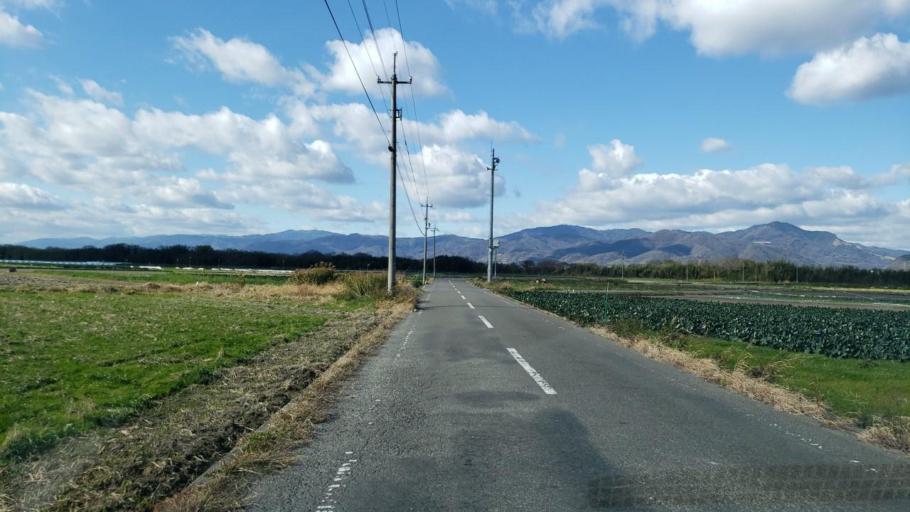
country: JP
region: Tokushima
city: Kamojimacho-jogejima
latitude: 34.0723
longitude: 134.3011
